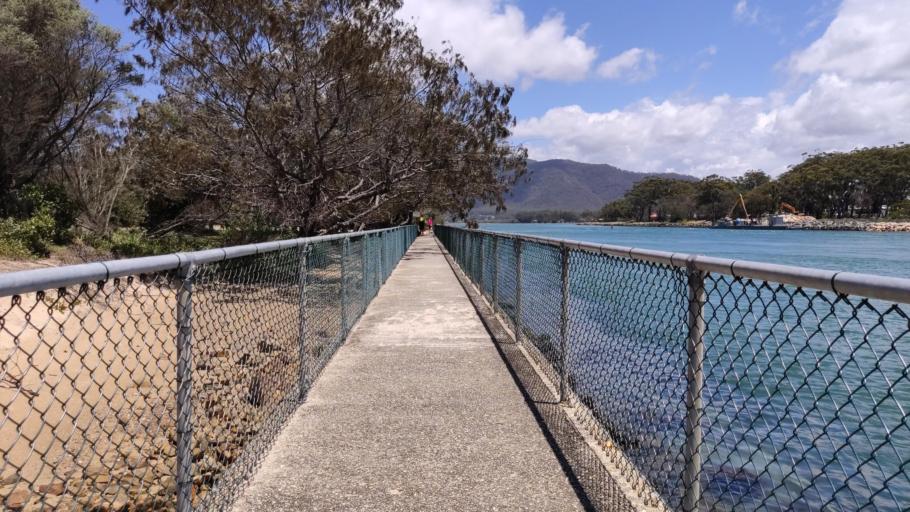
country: AU
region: New South Wales
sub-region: Port Macquarie-Hastings
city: North Haven
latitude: -31.6393
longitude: 152.8285
